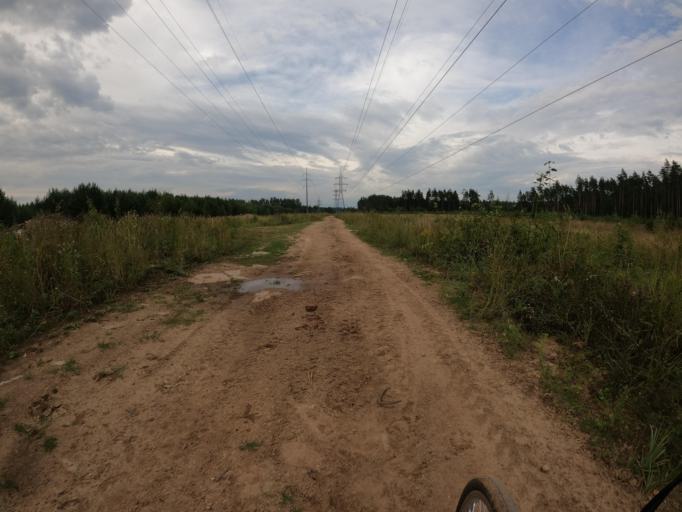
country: RU
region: Moskovskaya
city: Rodniki
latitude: 55.6760
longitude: 38.0851
